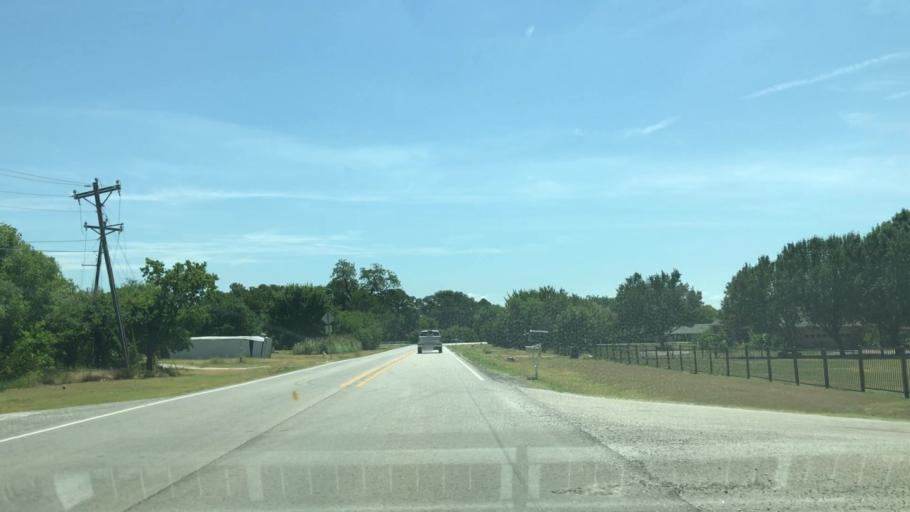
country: US
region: Texas
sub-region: Collin County
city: Lucas
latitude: 33.1102
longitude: -96.6006
